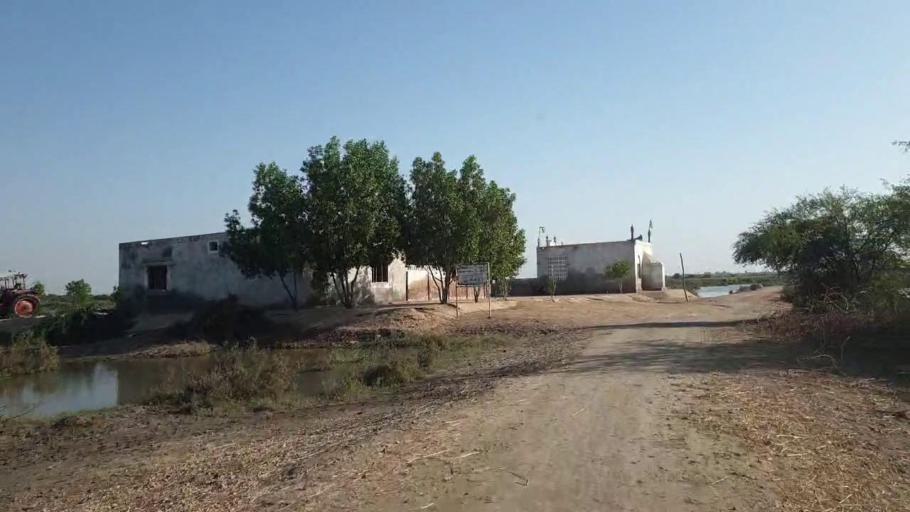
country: PK
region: Sindh
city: Badin
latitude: 24.5916
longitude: 68.9128
